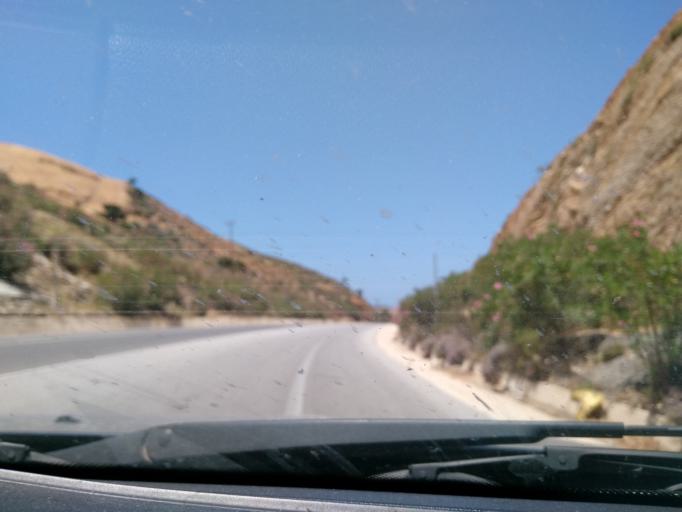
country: GR
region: Crete
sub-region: Nomos Rethymnis
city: Anogeia
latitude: 35.3903
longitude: 24.9293
